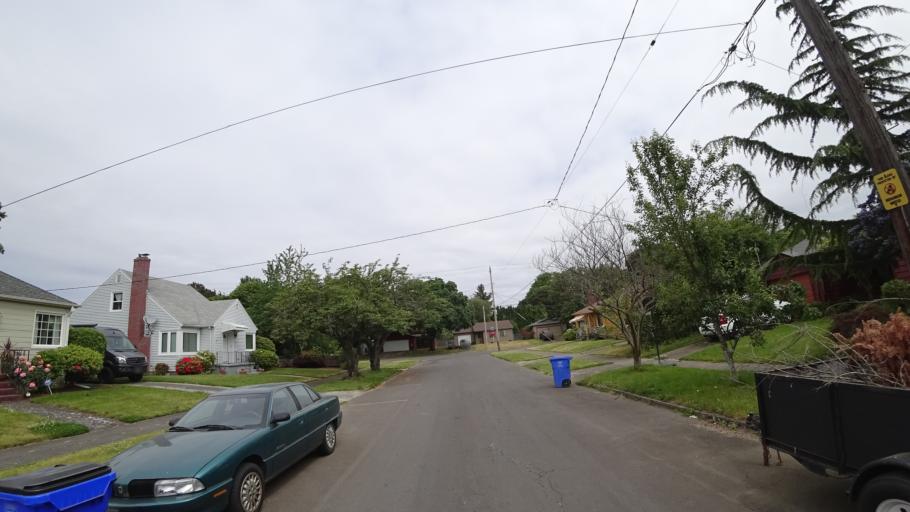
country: US
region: Oregon
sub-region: Multnomah County
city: Portland
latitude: 45.5713
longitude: -122.6393
